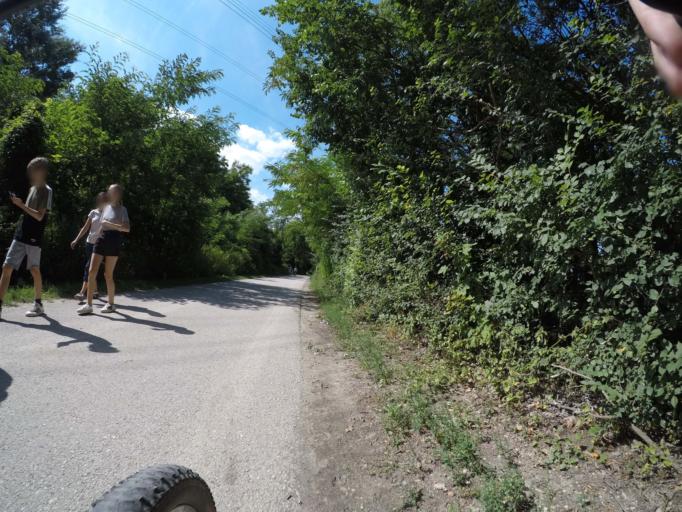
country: AT
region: Lower Austria
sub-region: Politischer Bezirk Ganserndorf
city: Gross-Enzersdorf
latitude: 48.1921
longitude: 16.5010
